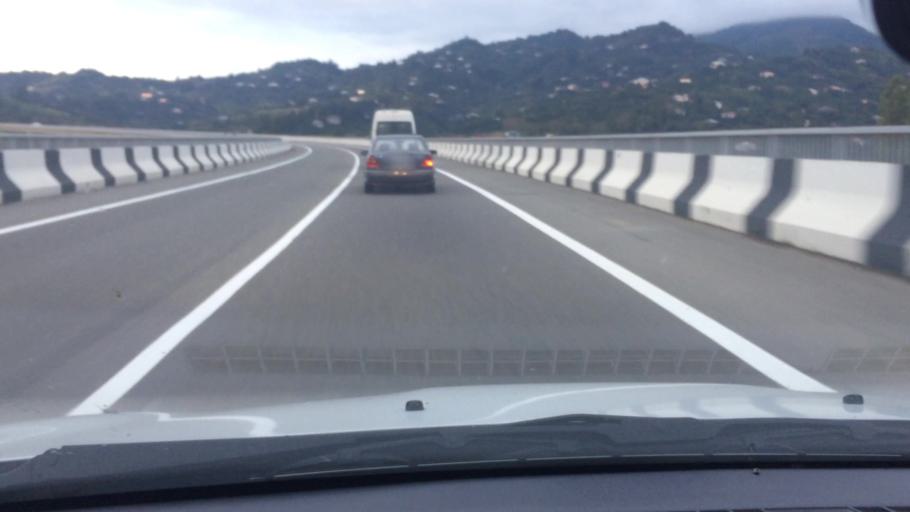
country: GE
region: Ajaria
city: Makhinjauri
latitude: 41.7115
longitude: 41.7499
